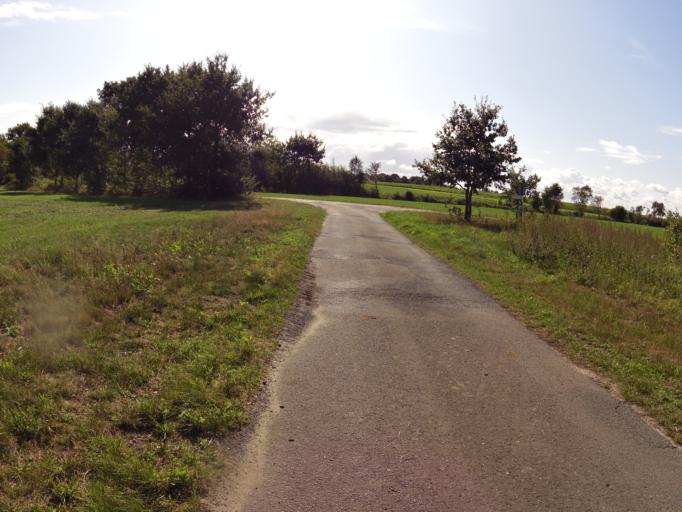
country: DE
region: Lower Saxony
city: Sandbostel
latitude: 53.3884
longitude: 9.1231
